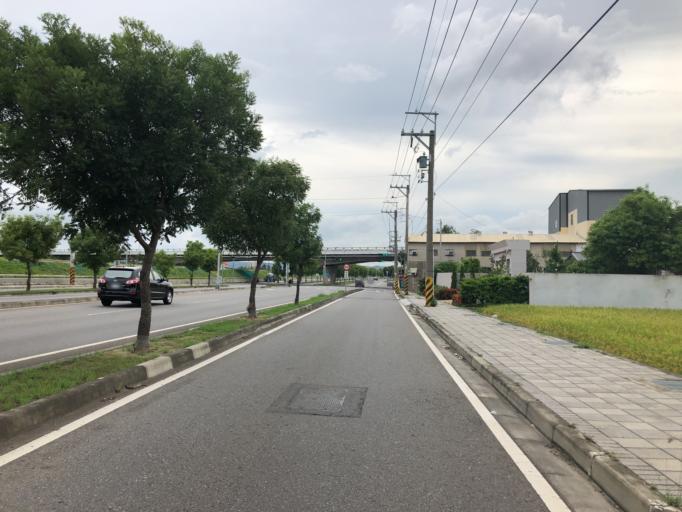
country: TW
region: Taiwan
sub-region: Taichung City
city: Taichung
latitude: 24.0845
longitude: 120.6729
